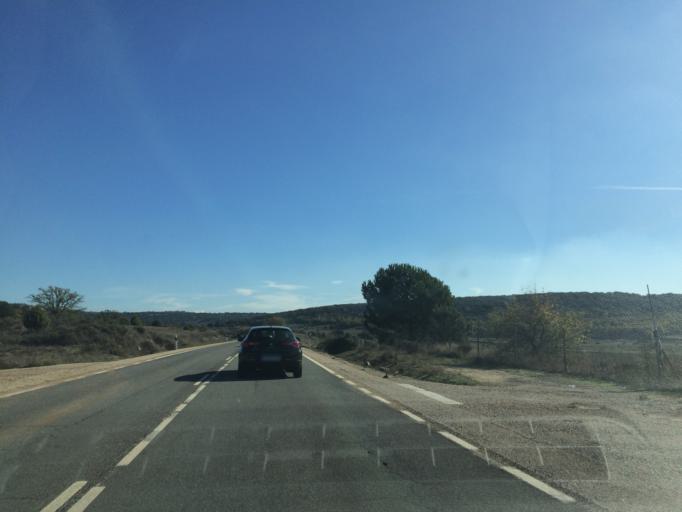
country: ES
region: Madrid
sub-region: Provincia de Madrid
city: Venturada
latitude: 40.7807
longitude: -3.6458
